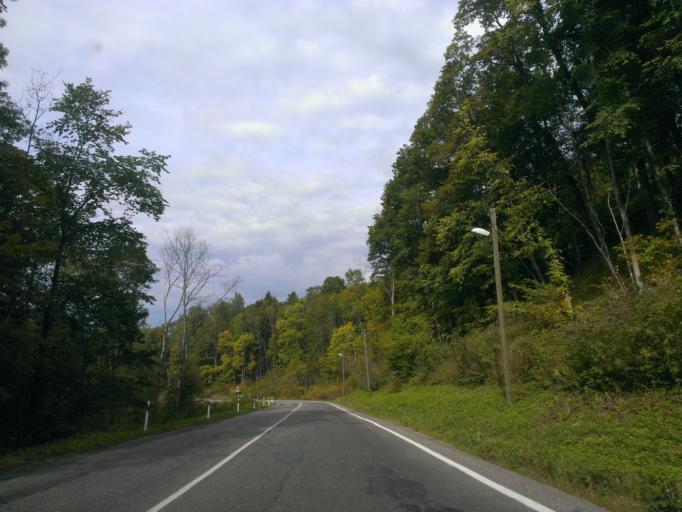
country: LV
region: Sigulda
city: Sigulda
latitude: 57.1649
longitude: 24.8491
